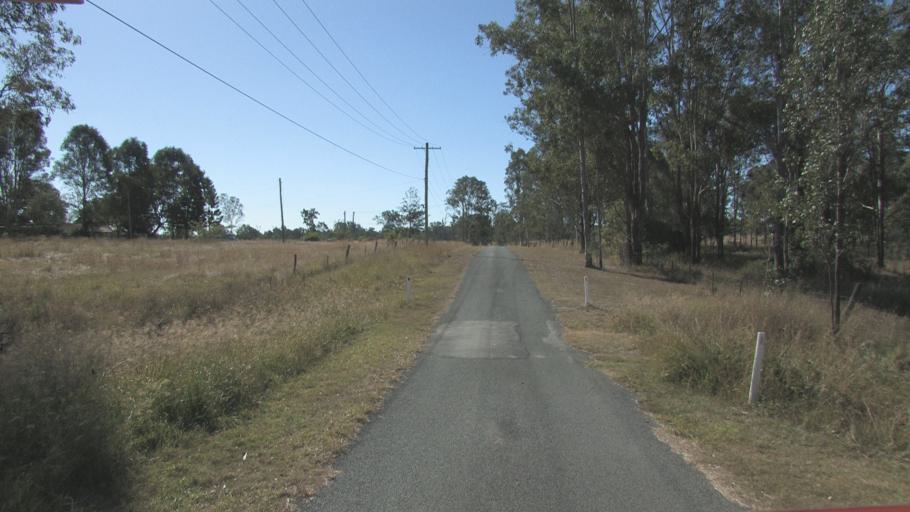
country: AU
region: Queensland
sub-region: Logan
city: North Maclean
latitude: -27.7754
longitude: 153.0251
